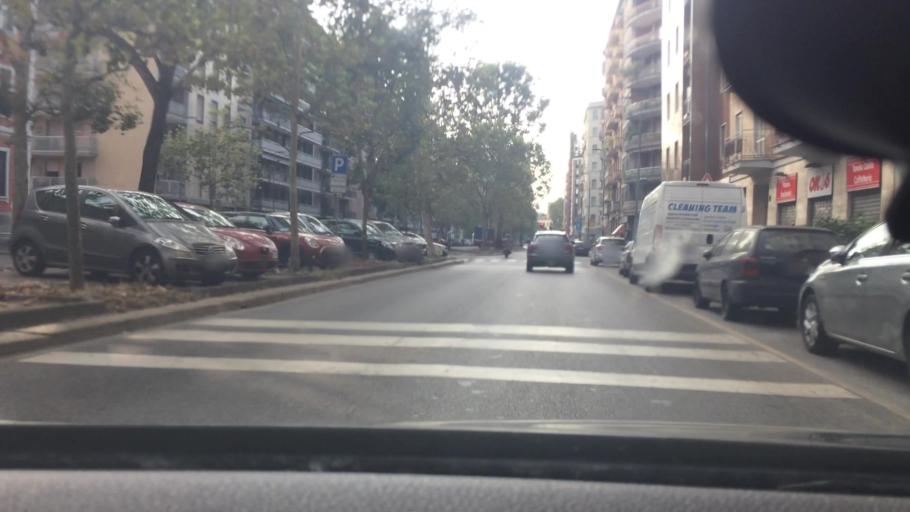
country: IT
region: Lombardy
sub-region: Citta metropolitana di Milano
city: Milano
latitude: 45.4876
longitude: 9.2129
